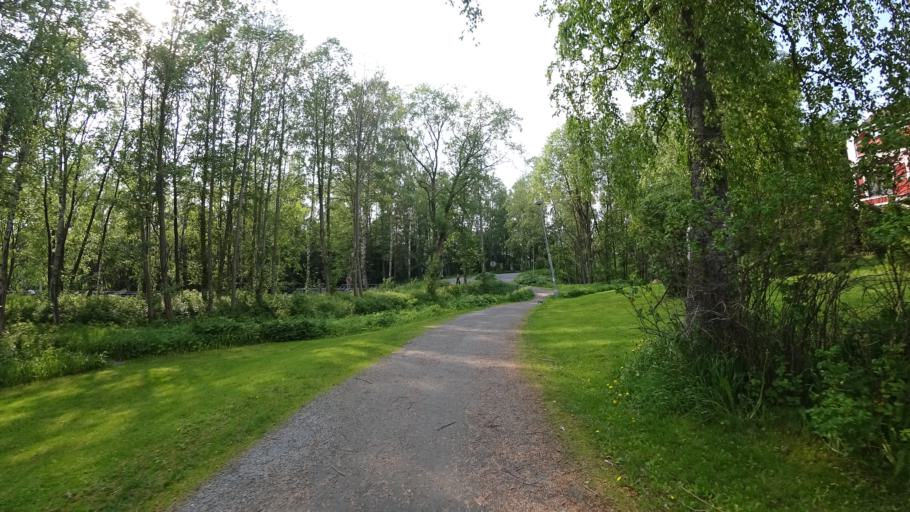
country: FI
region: Pirkanmaa
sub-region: Tampere
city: Pirkkala
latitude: 61.5038
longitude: 23.6977
